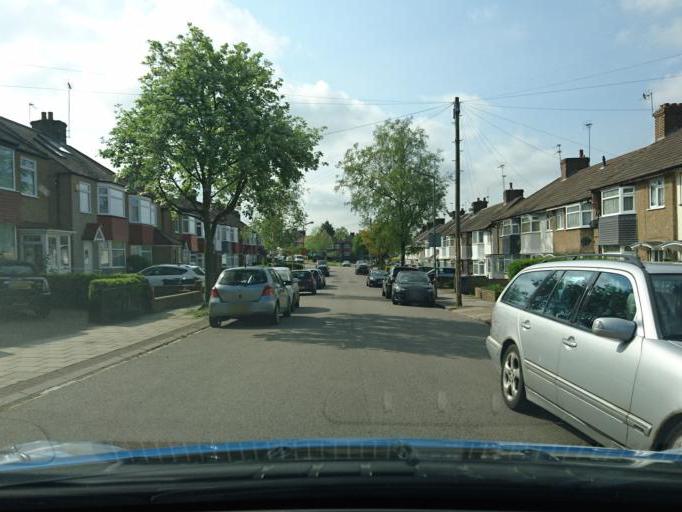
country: GB
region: England
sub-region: Greater London
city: Barnet
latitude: 51.6465
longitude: -0.1902
